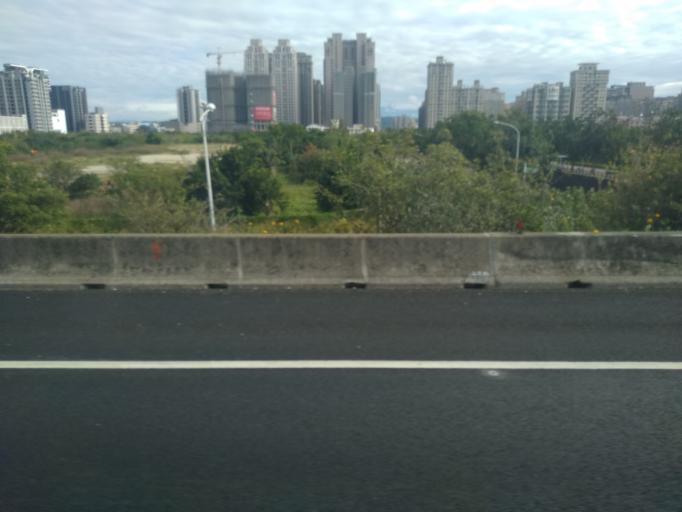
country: TW
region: Taiwan
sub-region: Hsinchu
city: Zhubei
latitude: 24.8292
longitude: 121.0198
